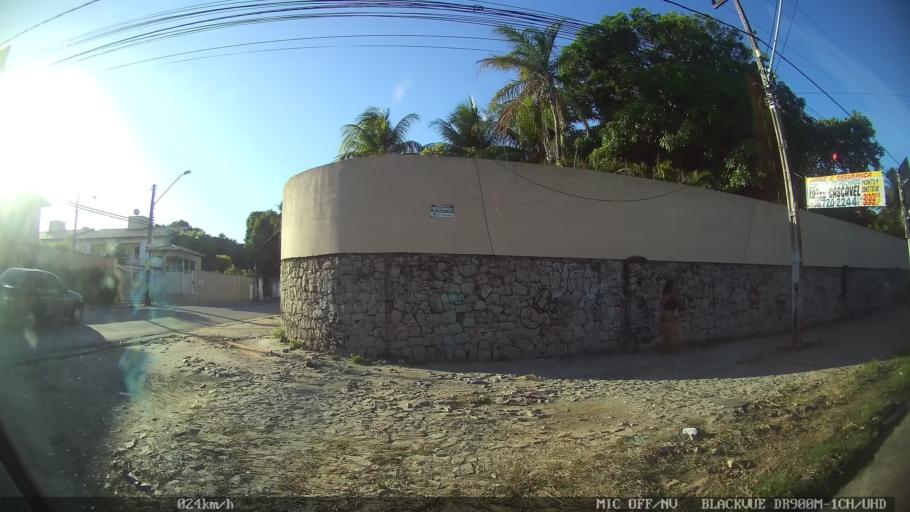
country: BR
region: Ceara
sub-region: Eusebio
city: Eusebio
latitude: -3.8238
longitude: -38.4793
